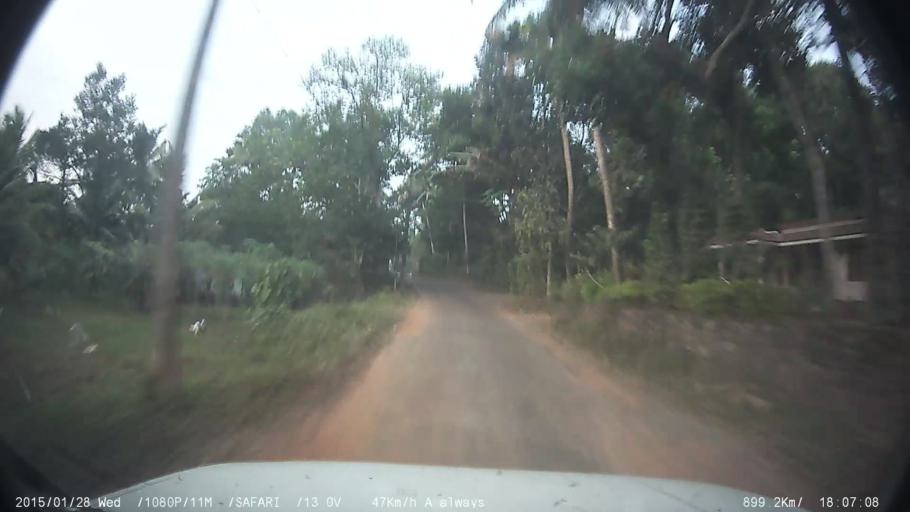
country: IN
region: Kerala
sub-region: Kottayam
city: Palackattumala
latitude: 9.7331
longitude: 76.5771
